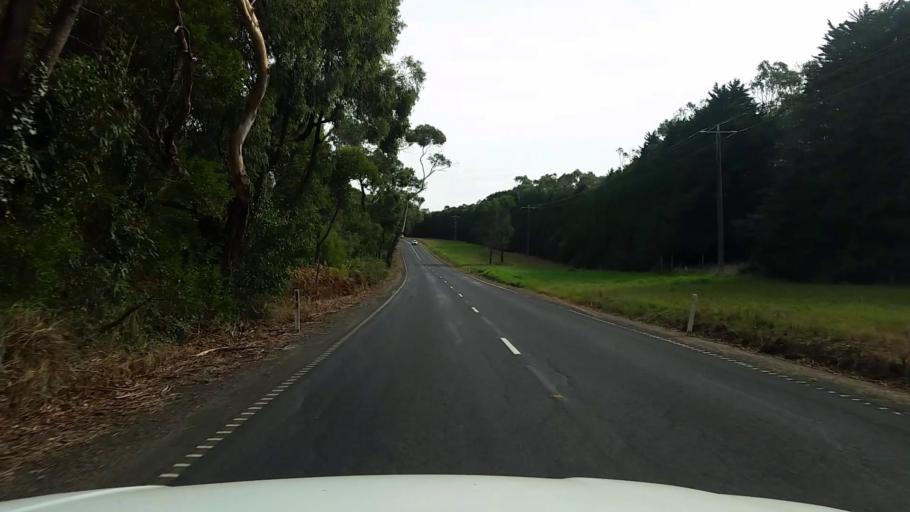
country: AU
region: Victoria
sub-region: Mornington Peninsula
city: Merricks
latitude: -38.3068
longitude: 145.0829
